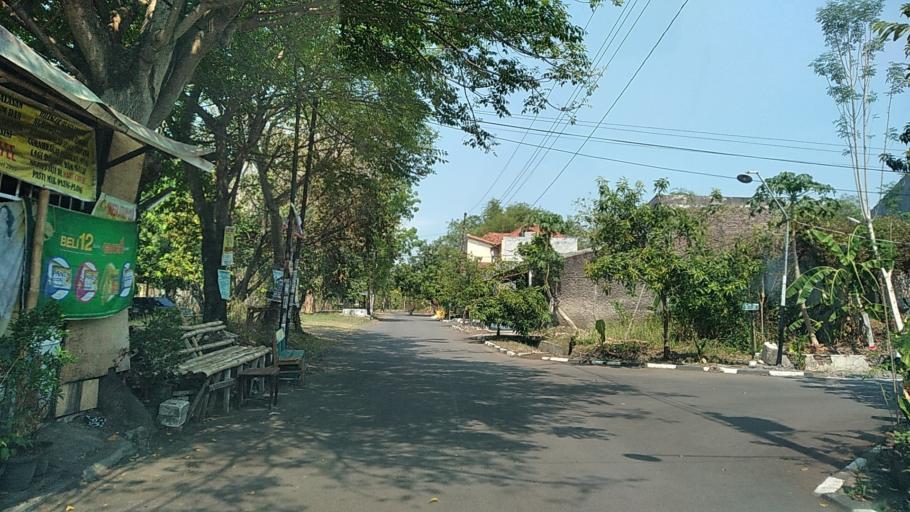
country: ID
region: Central Java
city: Mranggen
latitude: -7.0438
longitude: 110.4805
